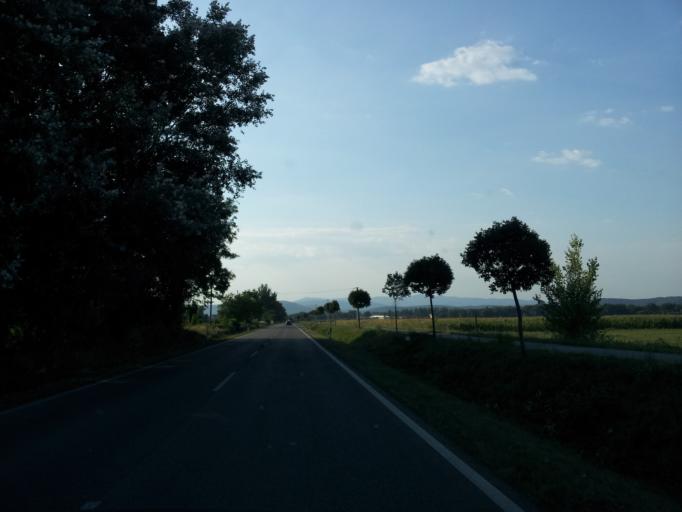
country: HU
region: Pest
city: Dunabogdany
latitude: 47.7780
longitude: 19.0531
